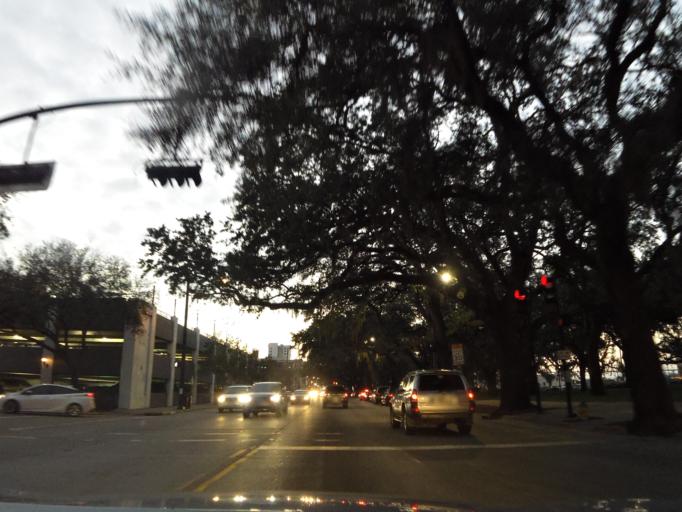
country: US
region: Georgia
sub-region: Chatham County
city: Savannah
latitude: 32.0792
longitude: -81.0847
